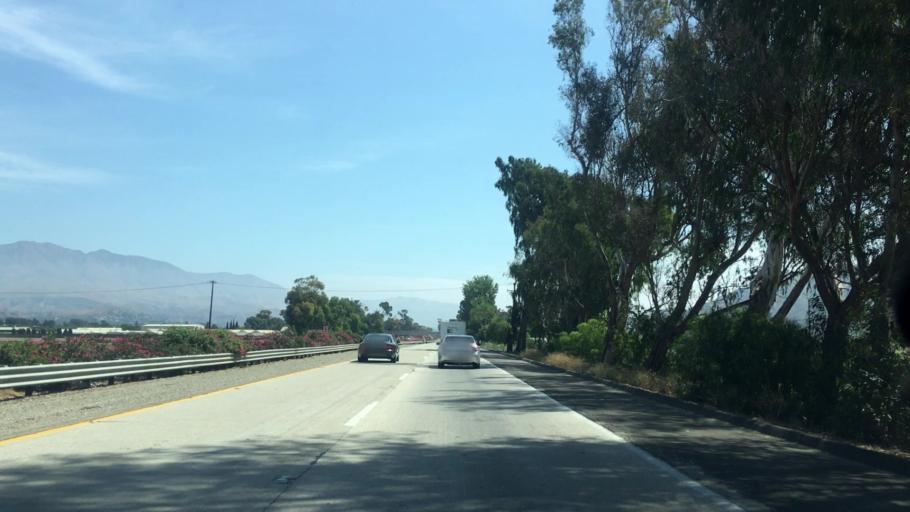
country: US
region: California
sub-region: Ventura County
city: Saticoy
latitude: 34.3181
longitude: -119.1083
